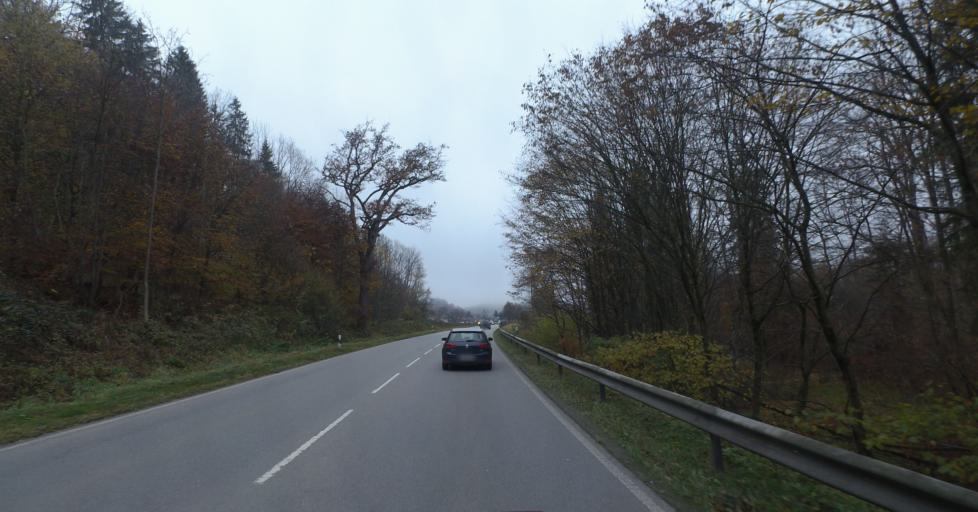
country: DE
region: Bavaria
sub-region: Upper Bavaria
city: Trostberg an der Alz
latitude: 48.0128
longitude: 12.5313
